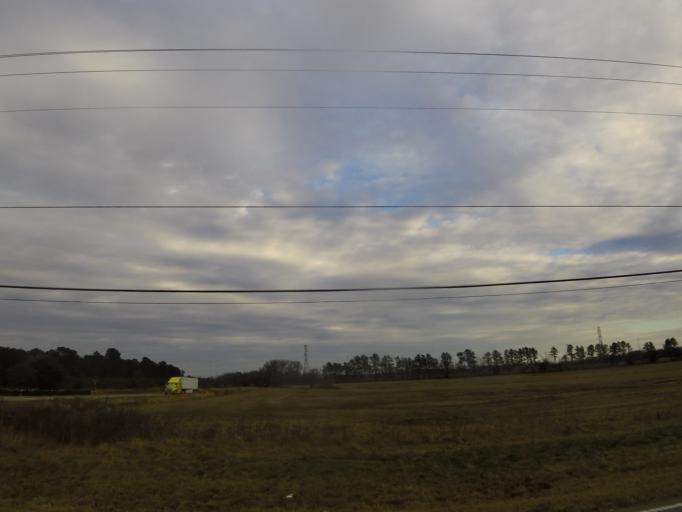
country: US
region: North Carolina
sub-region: Nash County
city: Rocky Mount
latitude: 36.0219
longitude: -77.7692
